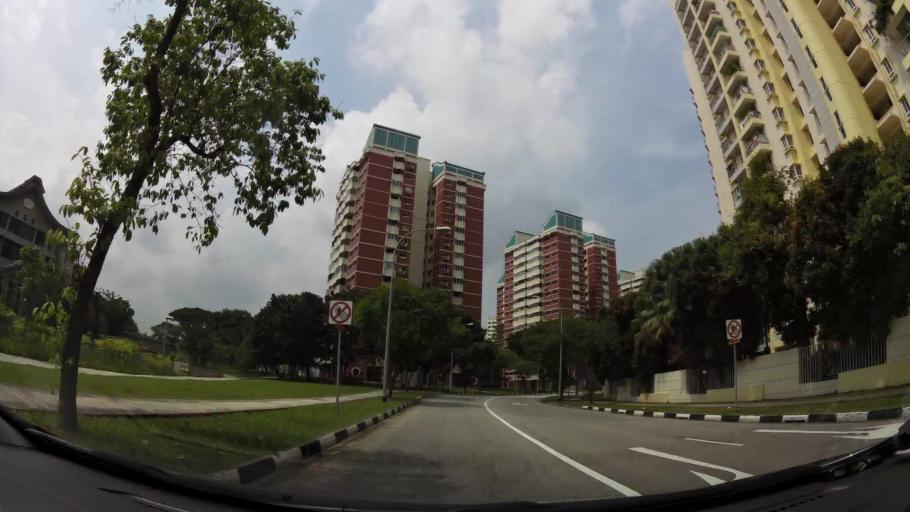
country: MY
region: Johor
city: Kampung Pasir Gudang Baru
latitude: 1.3734
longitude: 103.9398
